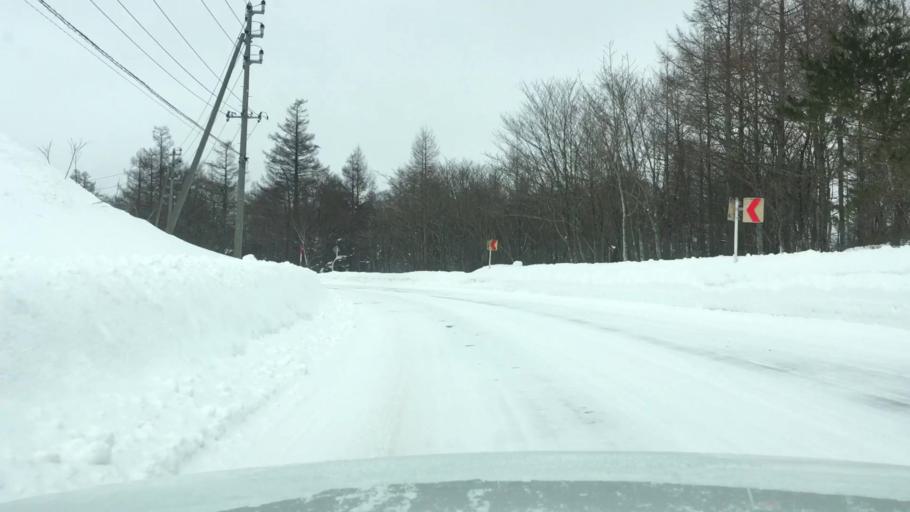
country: JP
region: Akita
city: Hanawa
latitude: 40.0022
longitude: 140.9850
